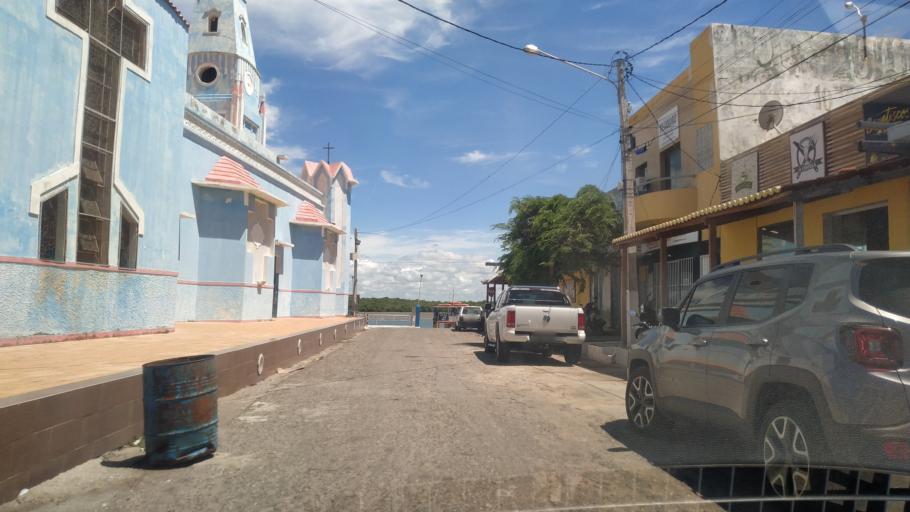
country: BR
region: Rio Grande do Norte
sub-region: Areia Branca
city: Areia Branca
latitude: -4.9560
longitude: -37.1362
